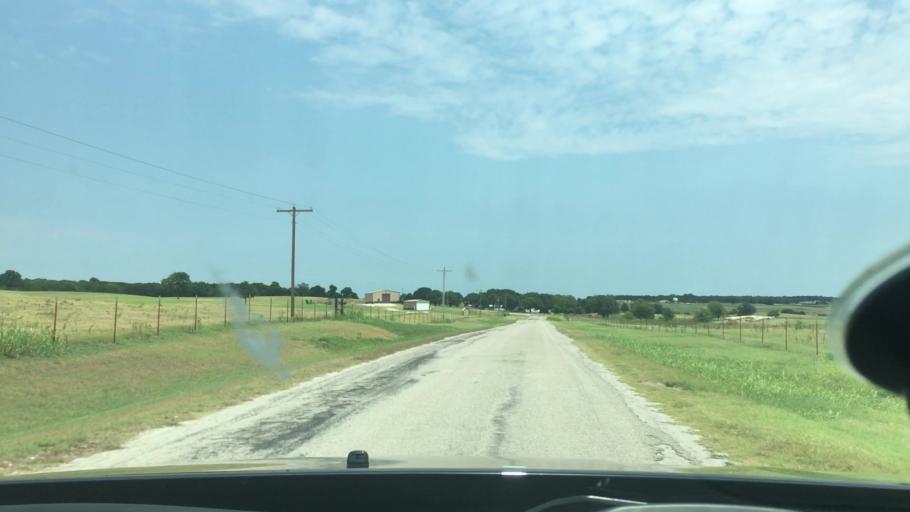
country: US
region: Texas
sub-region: Cooke County
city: Muenster
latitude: 33.8873
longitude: -97.3545
